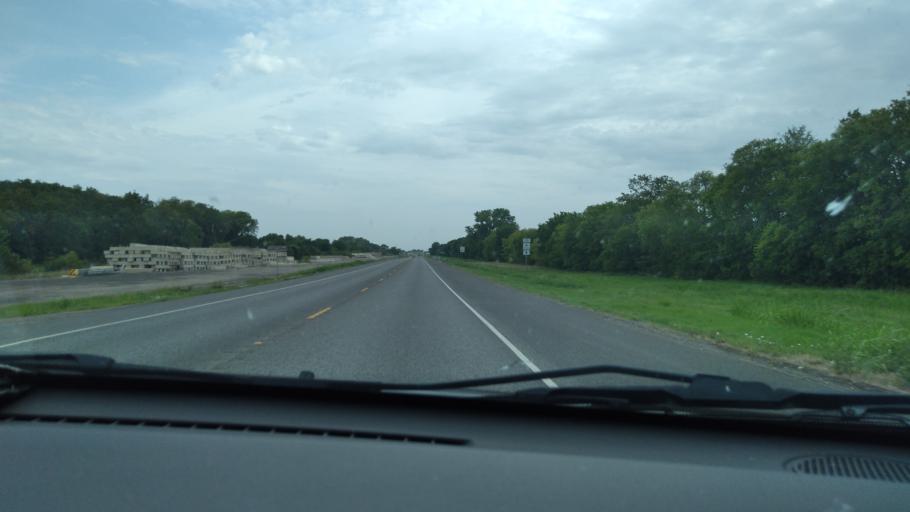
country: US
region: Texas
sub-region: McLennan County
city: Bellmead
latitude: 31.5637
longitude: -97.0675
